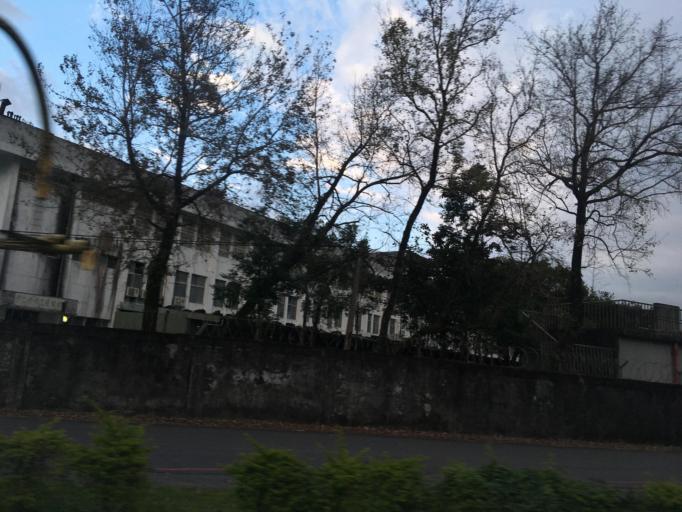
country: TW
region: Taiwan
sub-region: Yilan
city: Yilan
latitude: 24.7542
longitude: 121.7325
